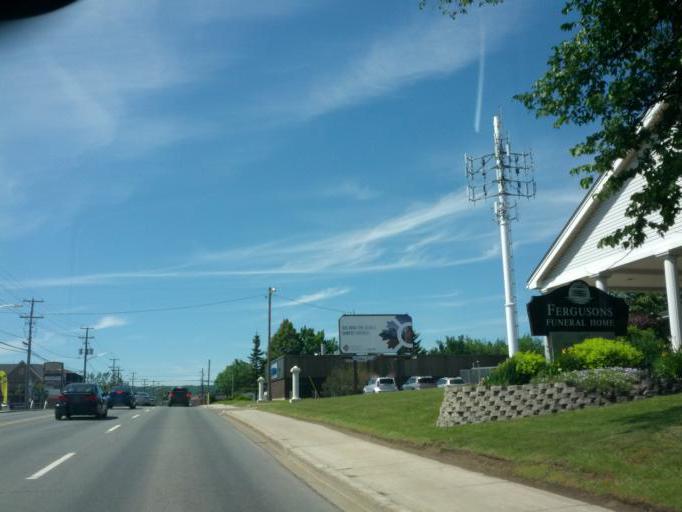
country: CA
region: New Brunswick
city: Moncton
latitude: 46.1182
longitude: -64.8415
